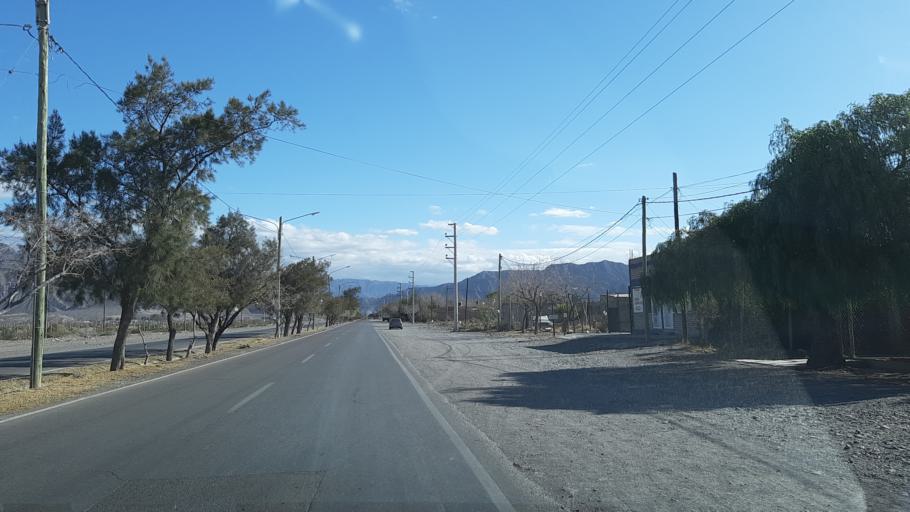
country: AR
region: San Juan
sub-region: Departamento de Rivadavia
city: Rivadavia
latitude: -31.5410
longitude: -68.6270
